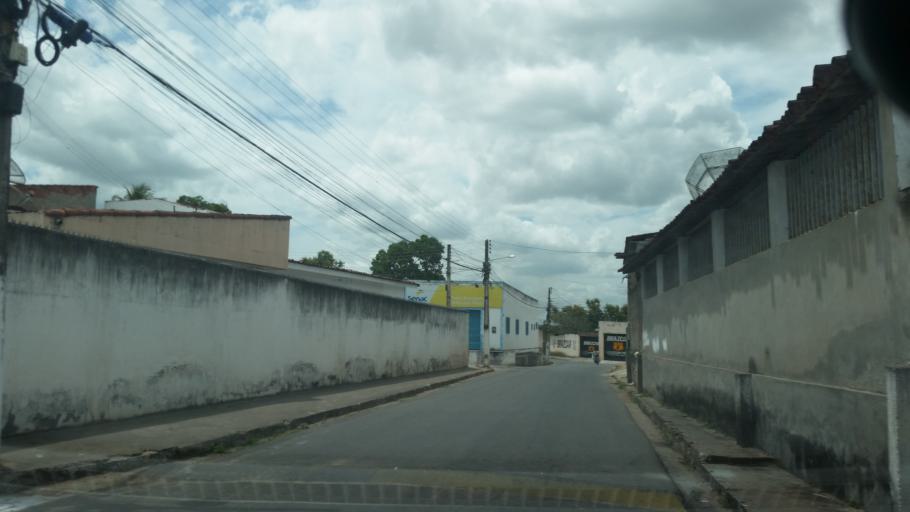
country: BR
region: Alagoas
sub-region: Uniao Dos Palmares
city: Uniao dos Palmares
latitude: -9.1607
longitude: -36.0351
